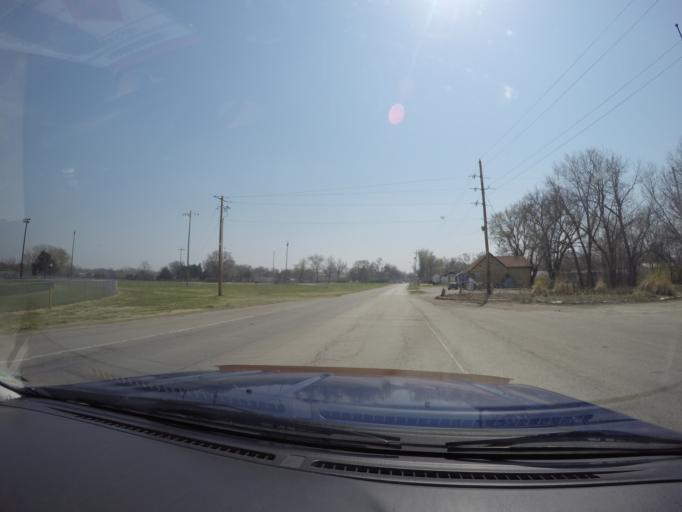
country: US
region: Kansas
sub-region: Morris County
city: Council Grove
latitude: 38.6685
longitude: -96.4877
